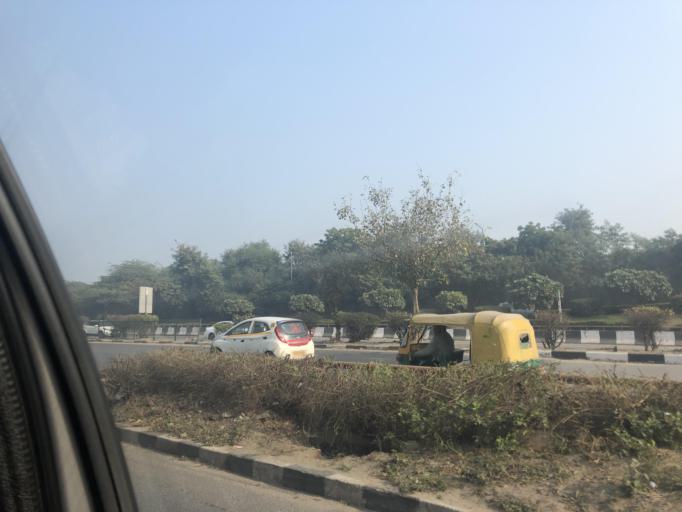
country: IN
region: NCT
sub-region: Central Delhi
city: Karol Bagh
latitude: 28.5975
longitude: 77.1640
